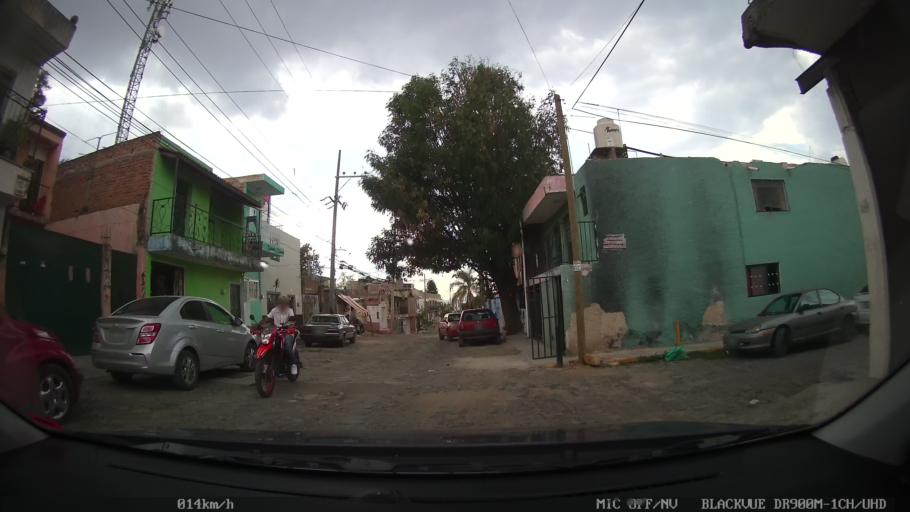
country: MX
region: Jalisco
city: Tonala
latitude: 20.6190
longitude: -103.2653
